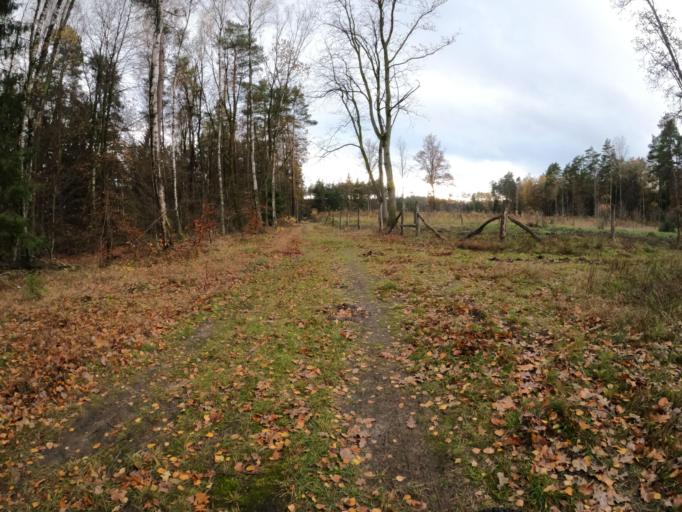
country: PL
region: West Pomeranian Voivodeship
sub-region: Powiat walecki
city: Tuczno
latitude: 53.2281
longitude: 16.2669
